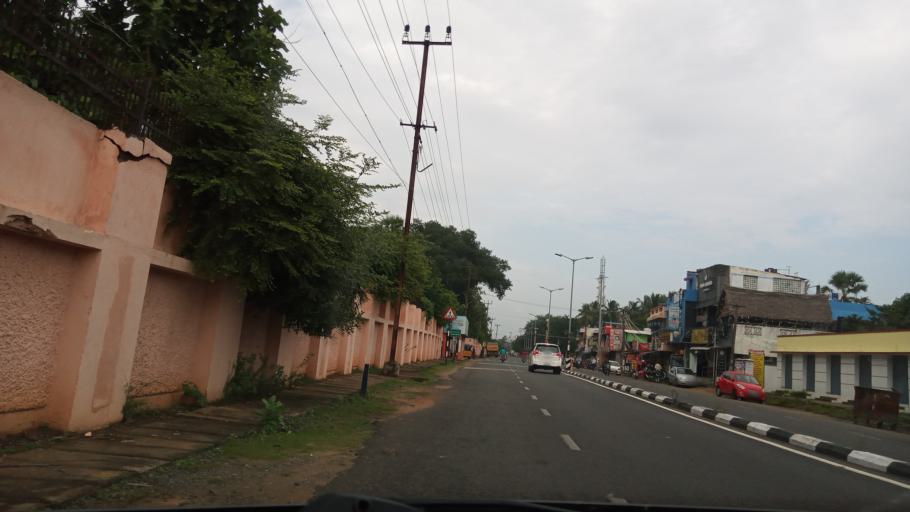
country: IN
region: Tamil Nadu
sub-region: Villupuram
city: Auroville
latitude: 12.0151
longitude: 79.8583
